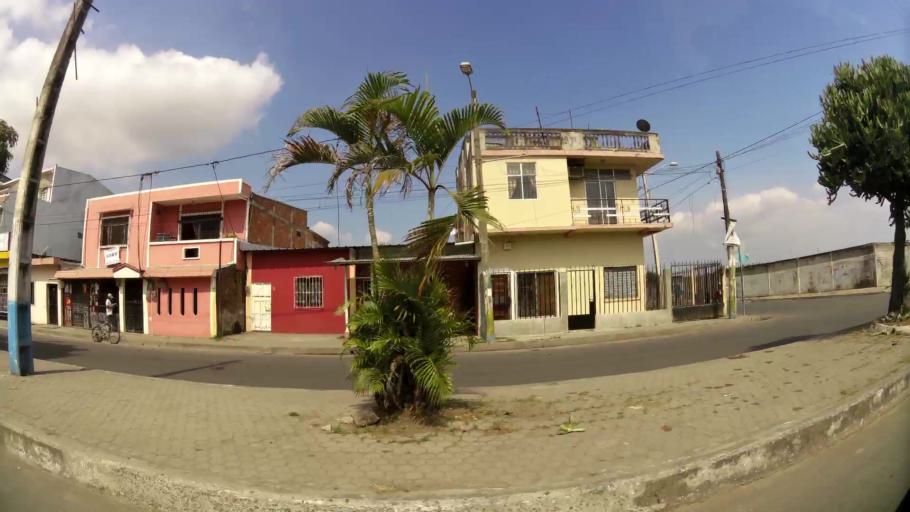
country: EC
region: Guayas
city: Eloy Alfaro
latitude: -2.1617
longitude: -79.8388
